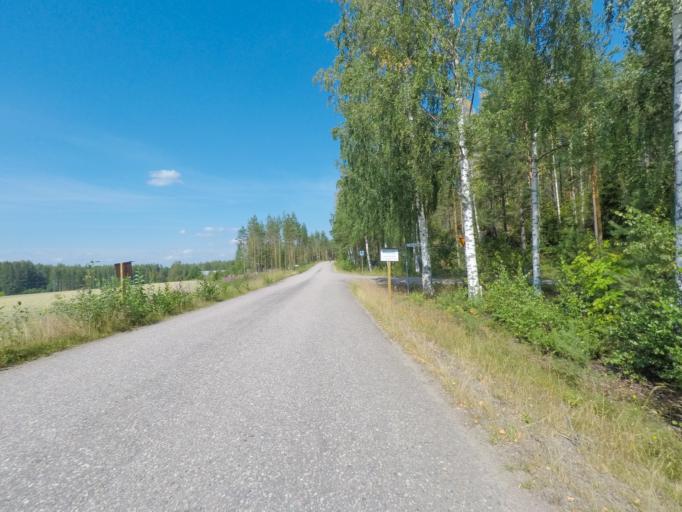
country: FI
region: Southern Savonia
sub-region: Mikkeli
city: Puumala
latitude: 61.4153
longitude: 28.0921
